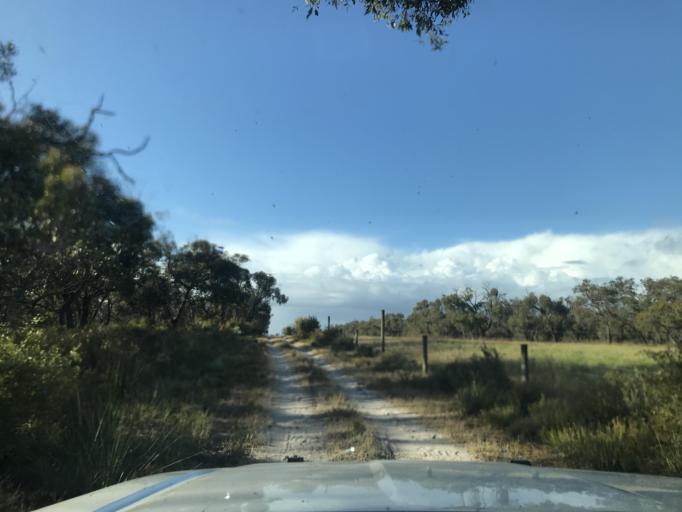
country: AU
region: South Australia
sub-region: Wattle Range
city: Penola
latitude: -37.1288
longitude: 141.3352
